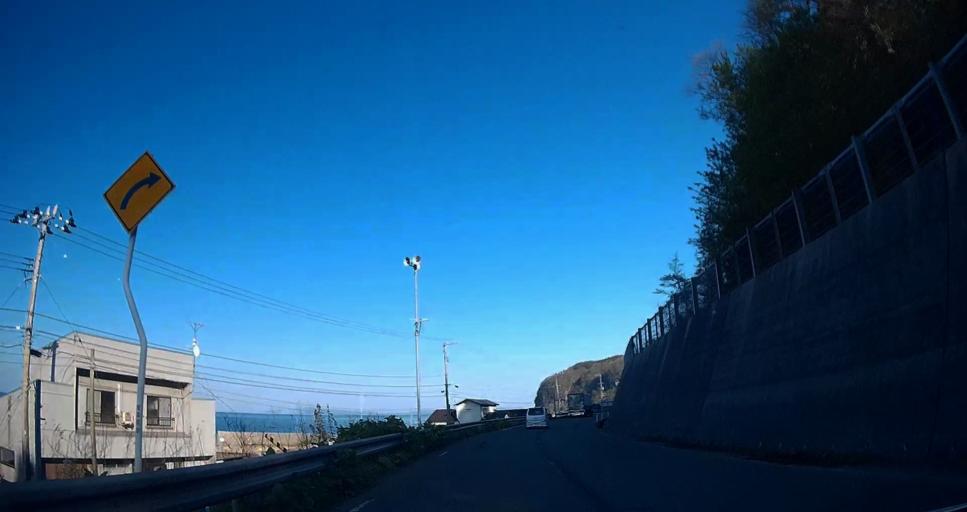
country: JP
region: Aomori
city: Mutsu
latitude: 41.4411
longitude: 141.1289
